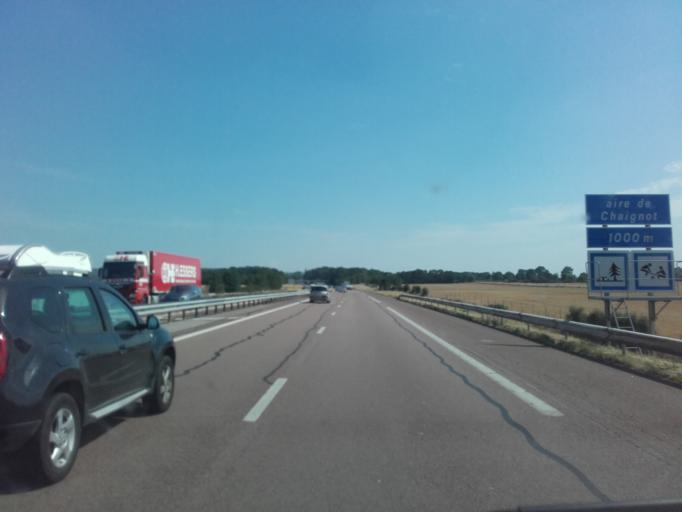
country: FR
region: Bourgogne
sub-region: Departement de la Cote-d'Or
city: Pouilly-en-Auxois
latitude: 47.2316
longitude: 4.5845
